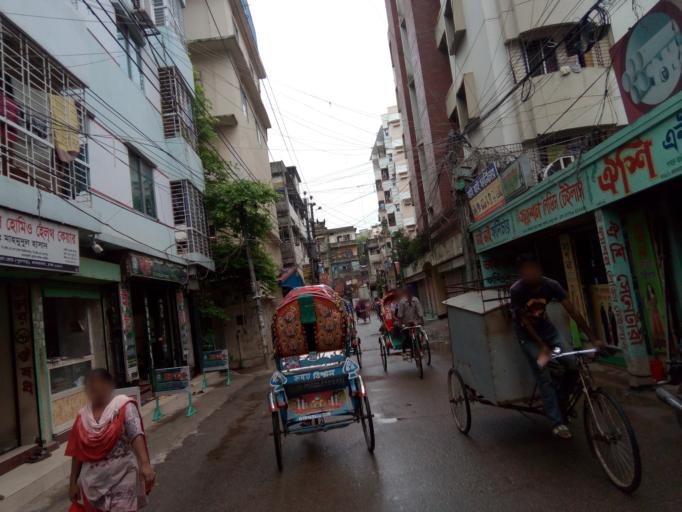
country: BD
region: Dhaka
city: Azimpur
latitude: 23.7508
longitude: 90.3631
